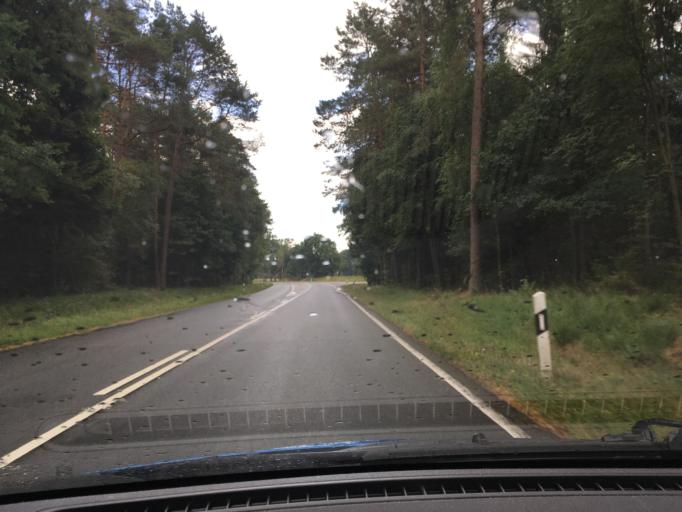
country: DE
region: Lower Saxony
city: Wietzendorf
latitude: 52.9664
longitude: 9.9565
